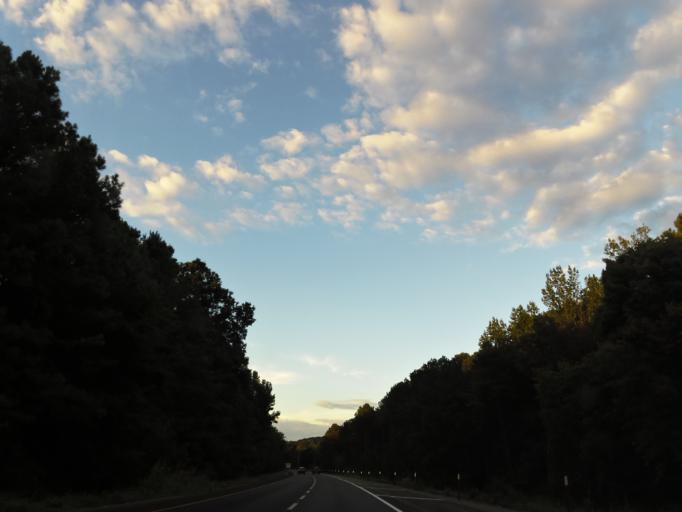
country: US
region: Tennessee
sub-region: Bradley County
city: Hopewell
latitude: 35.3306
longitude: -84.7587
